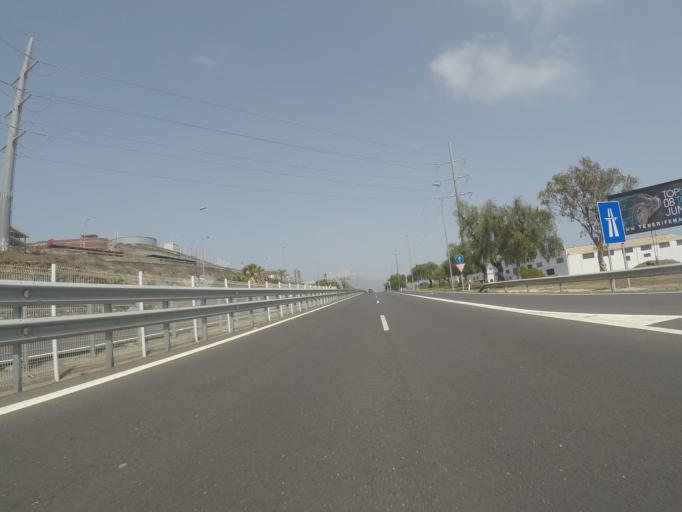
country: ES
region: Canary Islands
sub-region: Provincia de Santa Cruz de Tenerife
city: Santa Cruz de Tenerife
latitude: 28.4456
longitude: -16.2761
